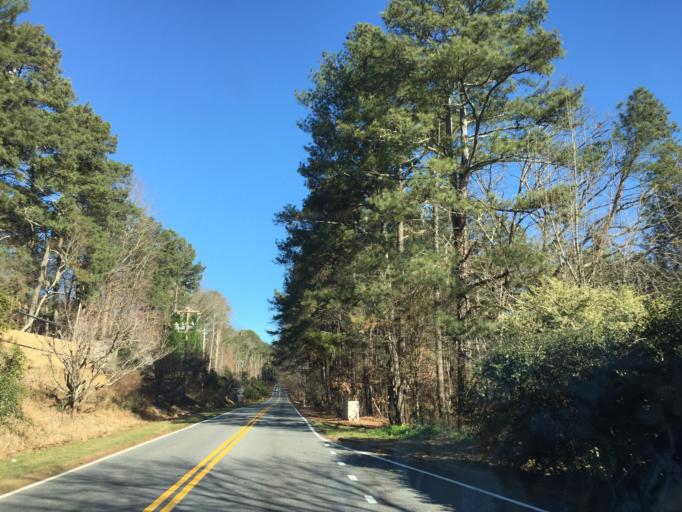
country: US
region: Georgia
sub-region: Gwinnett County
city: Norcross
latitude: 33.9937
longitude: -84.2587
